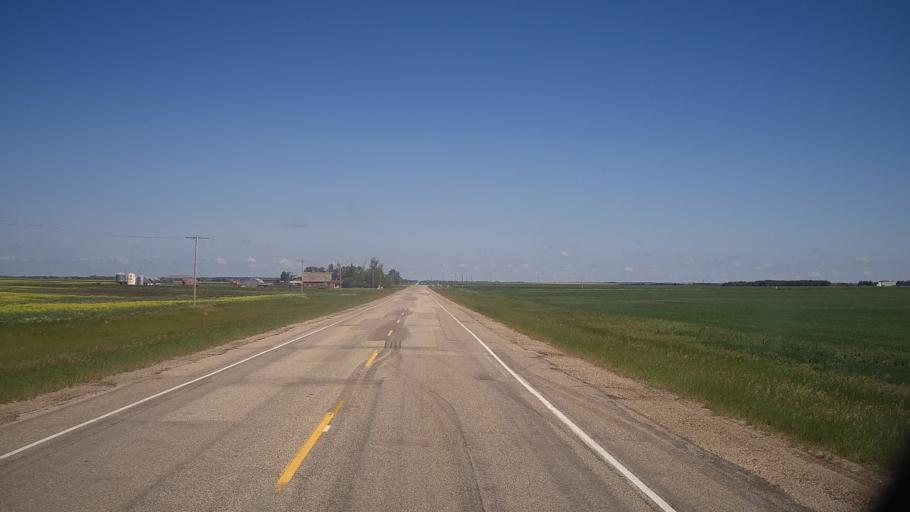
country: CA
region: Saskatchewan
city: Saskatoon
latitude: 51.9851
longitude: -106.0754
